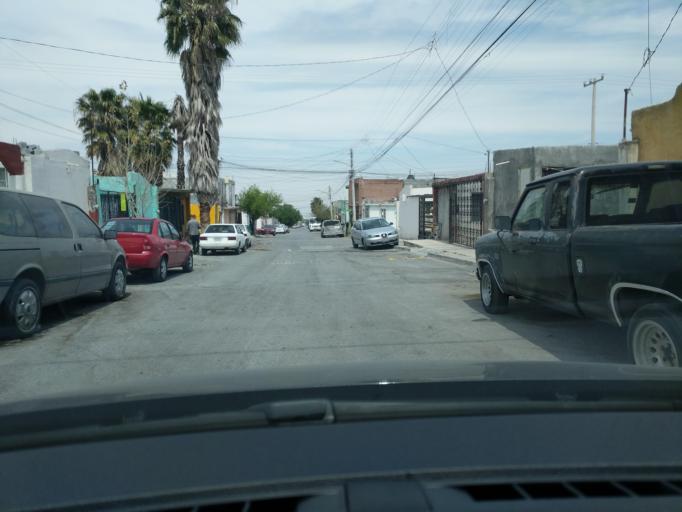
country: MX
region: Coahuila
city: Saltillo
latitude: 25.4078
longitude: -100.9380
